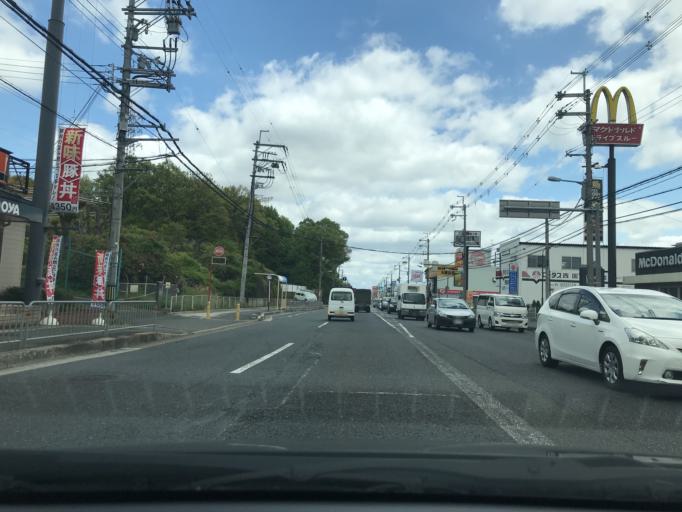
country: JP
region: Osaka
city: Mino
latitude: 34.8359
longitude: 135.5160
